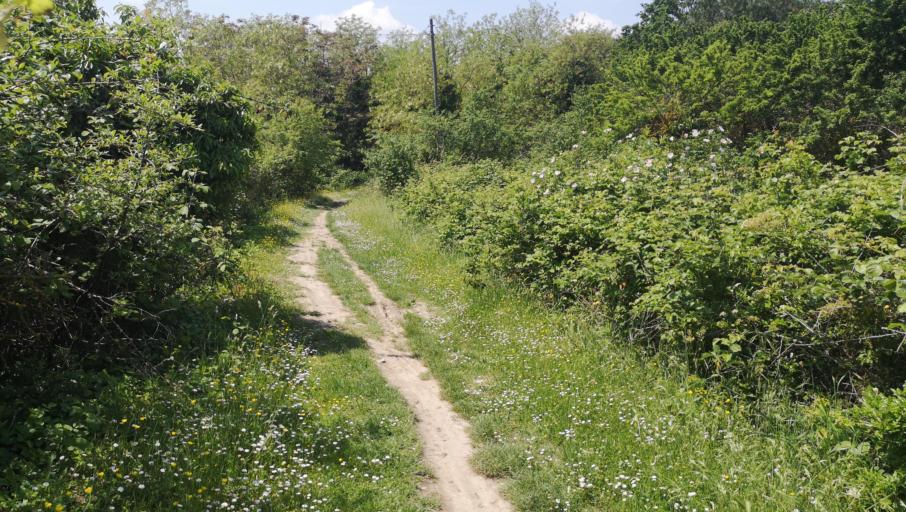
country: IT
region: Emilia-Romagna
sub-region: Provincia di Ravenna
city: Fosso Ghiaia
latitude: 44.3562
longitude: 12.2902
